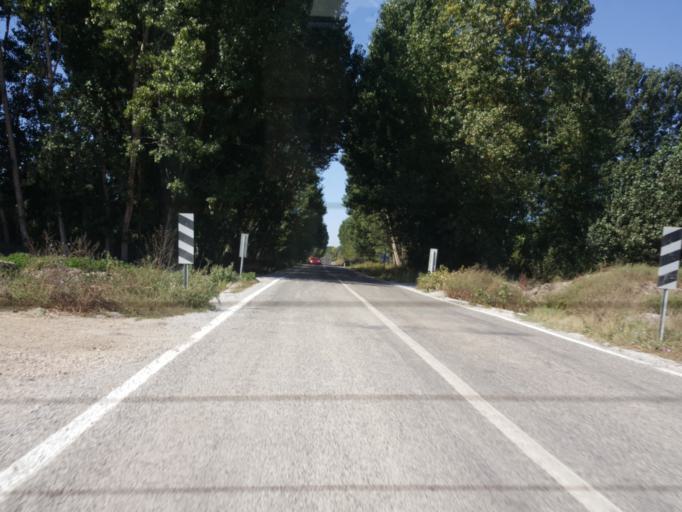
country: TR
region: Tokat
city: Pazar
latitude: 40.2679
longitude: 36.1949
